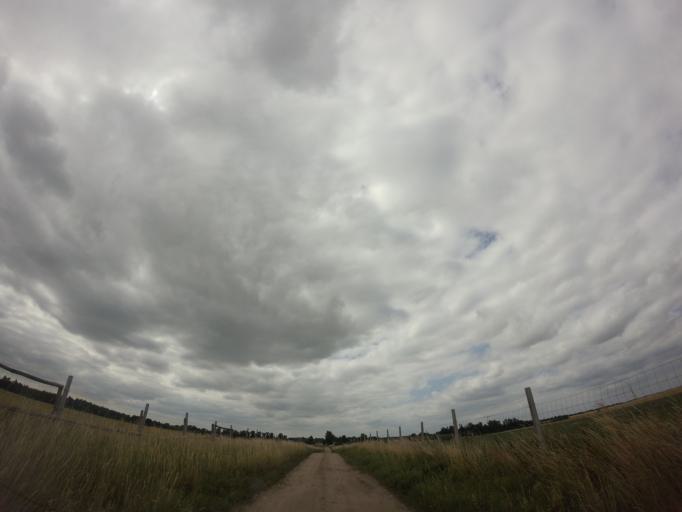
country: PL
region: Lubusz
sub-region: Powiat strzelecko-drezdenecki
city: Strzelce Krajenskie
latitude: 52.9103
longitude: 15.5993
